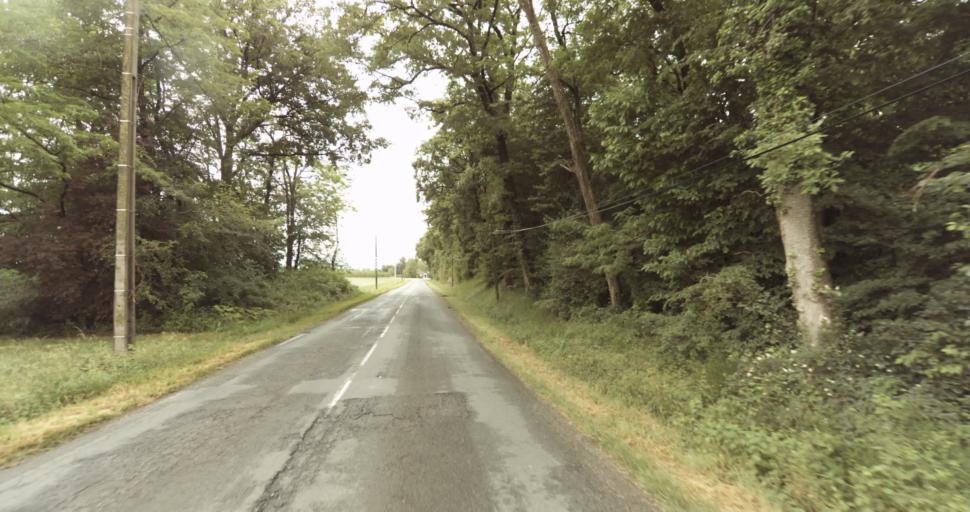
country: FR
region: Aquitaine
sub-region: Departement de la Dordogne
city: Beaumont-du-Perigord
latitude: 44.7293
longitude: 0.7899
